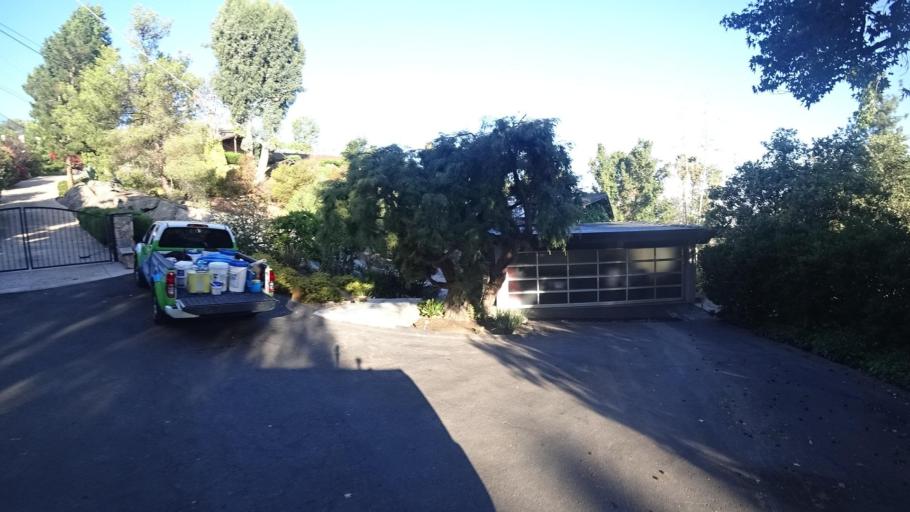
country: US
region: California
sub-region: San Diego County
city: Casa de Oro-Mount Helix
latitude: 32.7726
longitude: -116.9679
